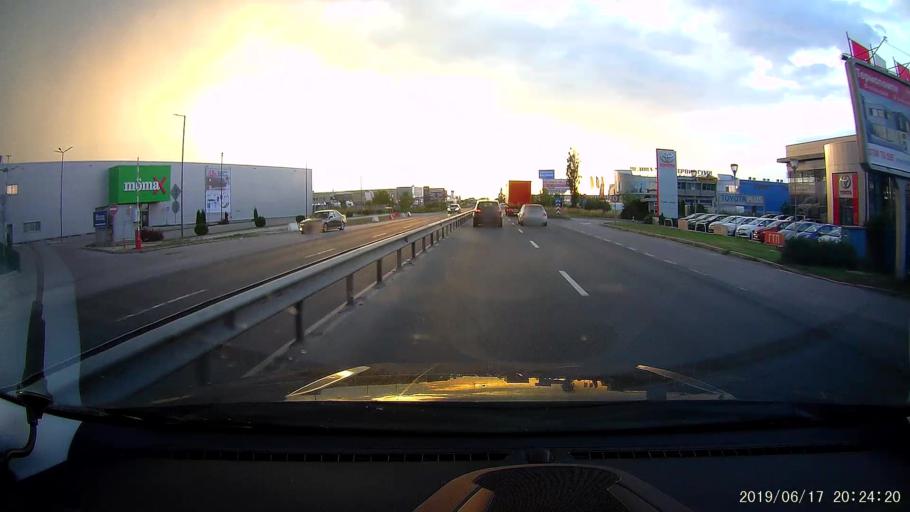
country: BG
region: Sofiya
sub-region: Obshtina Bozhurishte
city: Bozhurishte
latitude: 42.7402
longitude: 23.2381
